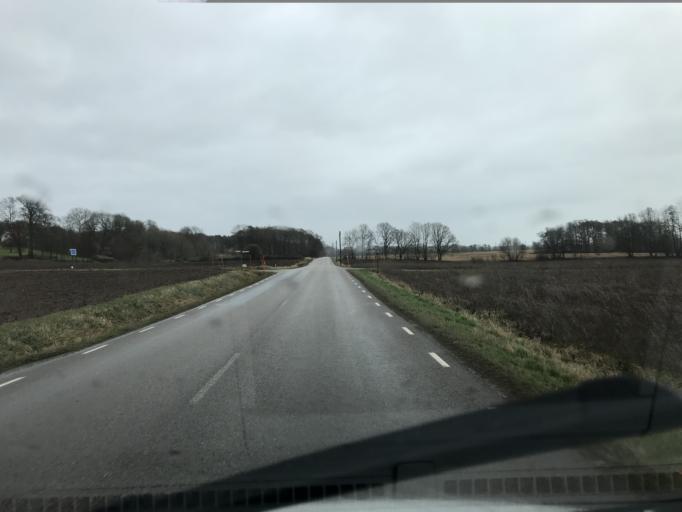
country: SE
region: Skane
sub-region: Bastads Kommun
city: Forslov
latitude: 56.3416
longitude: 12.8724
